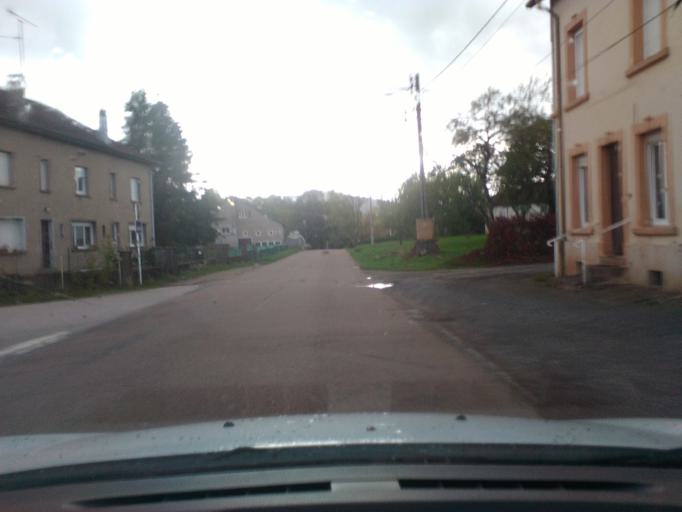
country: FR
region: Lorraine
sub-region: Departement des Vosges
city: Saint-Die-des-Vosges
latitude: 48.3073
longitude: 6.9569
